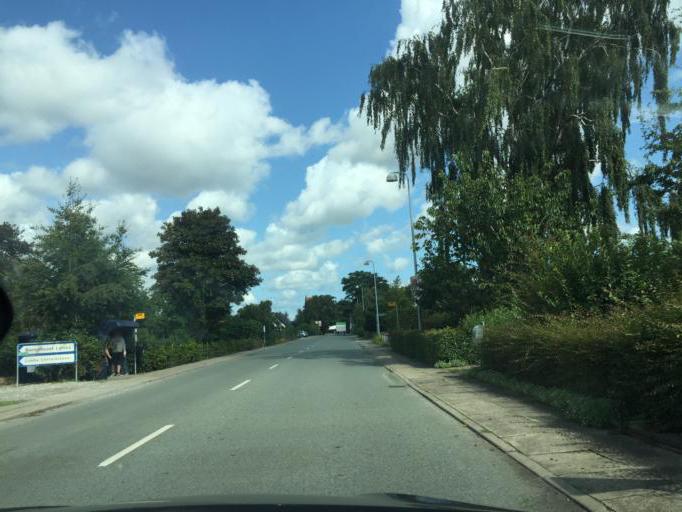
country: DK
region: South Denmark
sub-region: Odense Kommune
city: Stige
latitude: 55.4542
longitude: 10.3763
